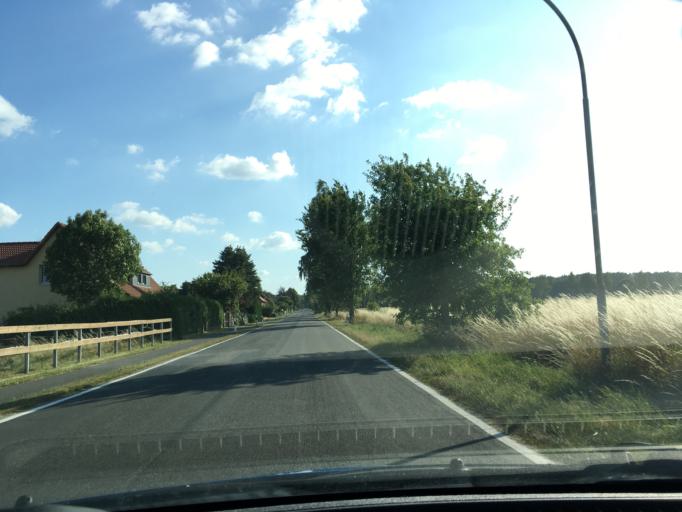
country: DE
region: Lower Saxony
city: Dahlenburg
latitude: 53.1736
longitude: 10.7082
